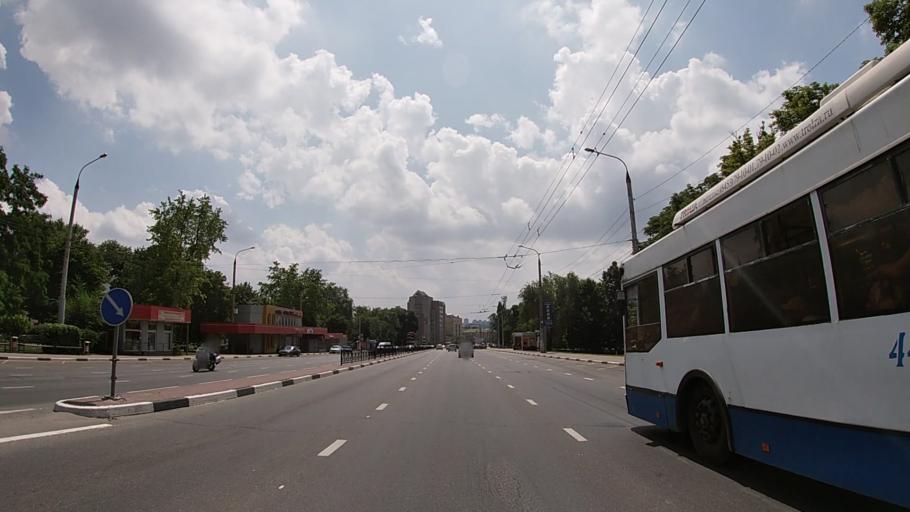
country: RU
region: Belgorod
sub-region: Belgorodskiy Rayon
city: Belgorod
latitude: 50.6059
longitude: 36.5804
